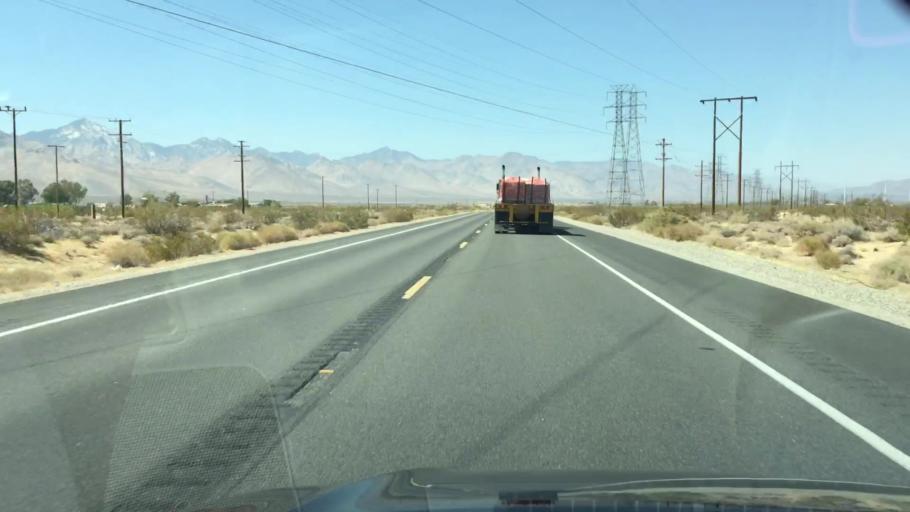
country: US
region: California
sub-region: Kern County
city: Inyokern
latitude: 35.6405
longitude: -117.7912
